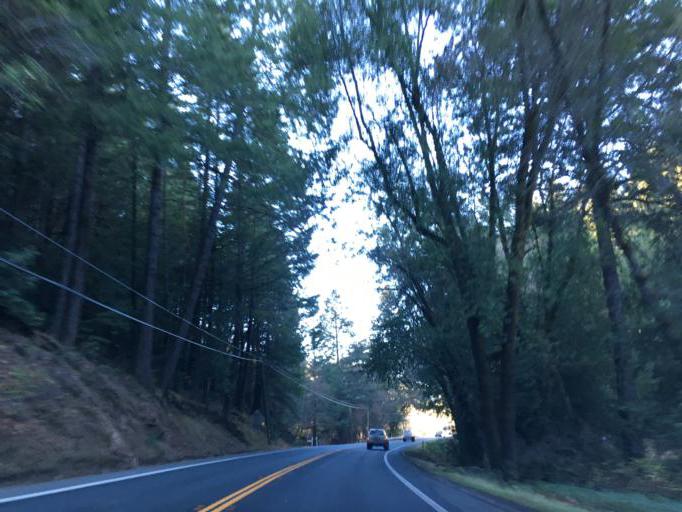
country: US
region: California
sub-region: Mendocino County
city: Brooktrails
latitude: 39.5094
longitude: -123.3847
